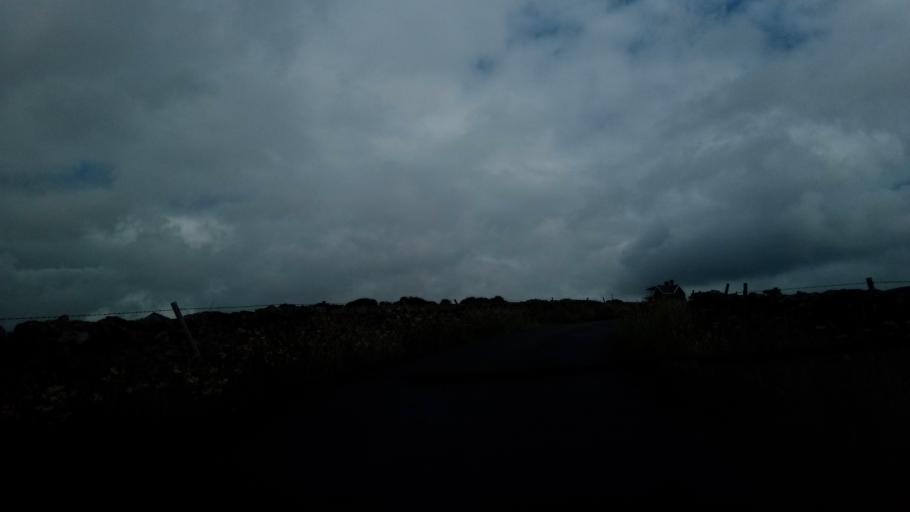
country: GB
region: England
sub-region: Cumbria
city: Sedbergh
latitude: 54.2824
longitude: -2.3688
